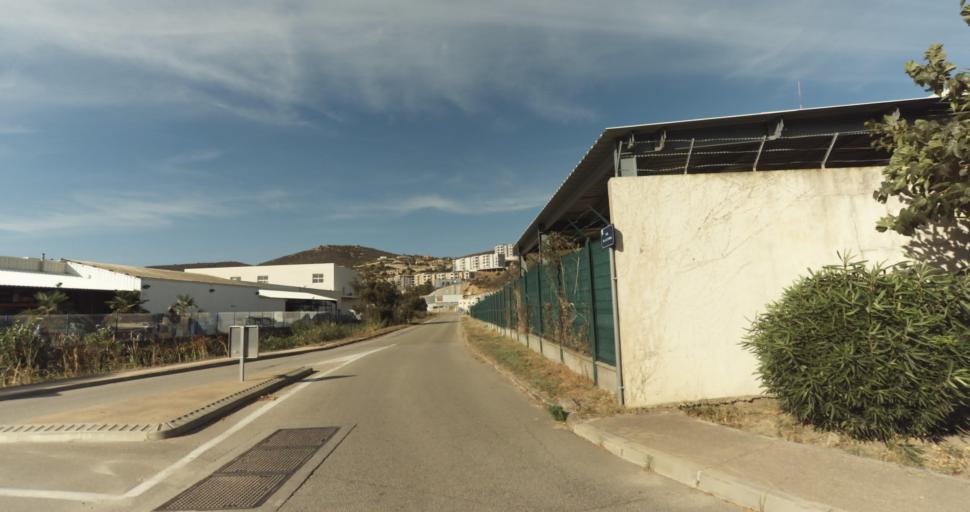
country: FR
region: Corsica
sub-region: Departement de la Corse-du-Sud
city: Afa
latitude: 41.9294
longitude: 8.7905
